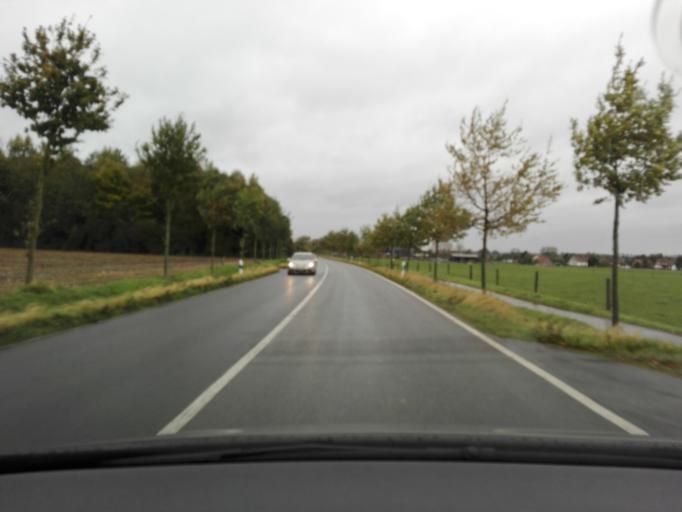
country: DE
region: North Rhine-Westphalia
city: Selm
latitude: 51.6606
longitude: 7.4945
